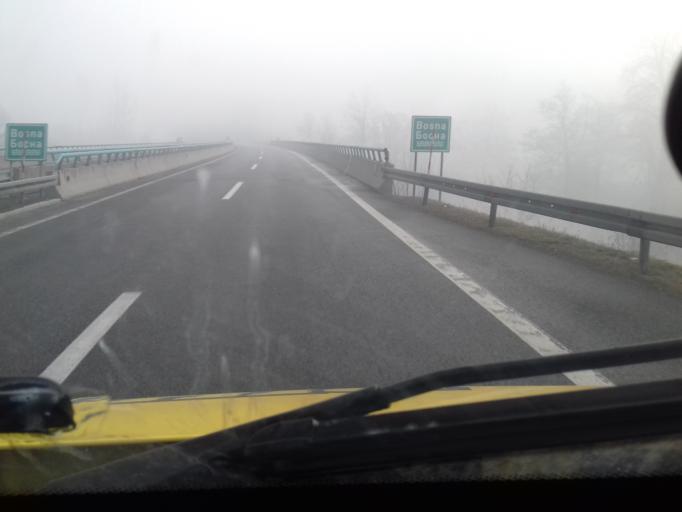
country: BA
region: Federation of Bosnia and Herzegovina
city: Ilijas
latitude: 43.9384
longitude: 18.2748
